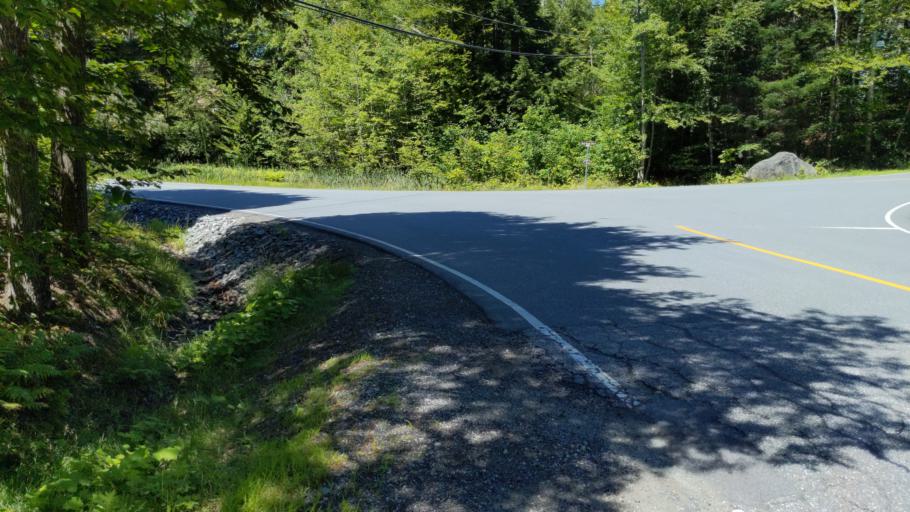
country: US
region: New Hampshire
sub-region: Sullivan County
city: Grantham
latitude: 43.5150
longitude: -72.1104
